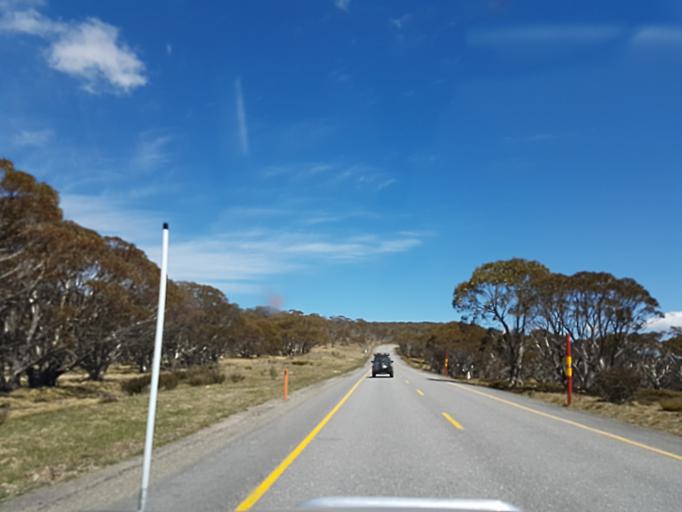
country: AU
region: Victoria
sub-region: Alpine
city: Mount Beauty
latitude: -37.0229
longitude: 147.2191
